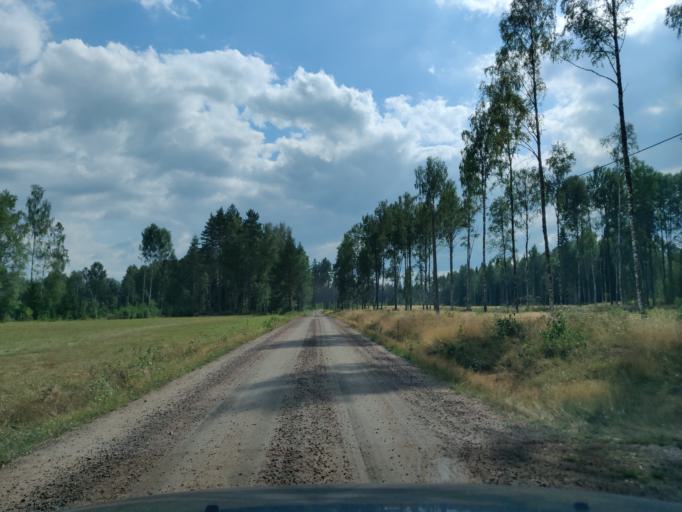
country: SE
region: Vaermland
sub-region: Hagfors Kommun
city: Hagfors
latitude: 59.9925
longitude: 13.5664
